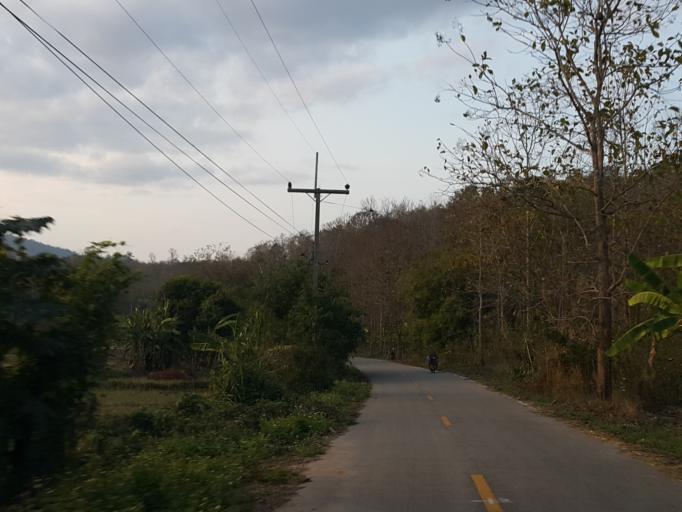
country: TH
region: Lampang
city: Mueang Pan
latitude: 18.7971
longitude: 99.4903
